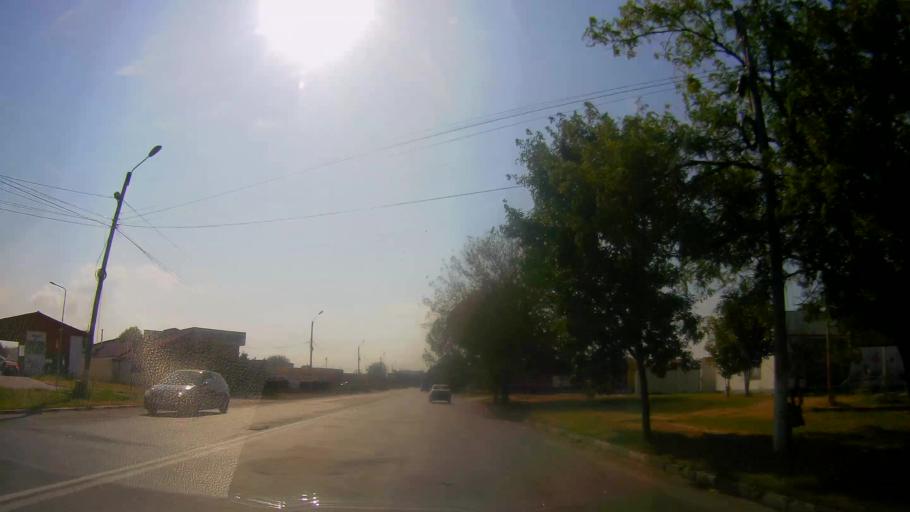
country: RO
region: Giurgiu
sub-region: Comuna Fratesti
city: Remus
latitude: 43.9145
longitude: 25.9724
